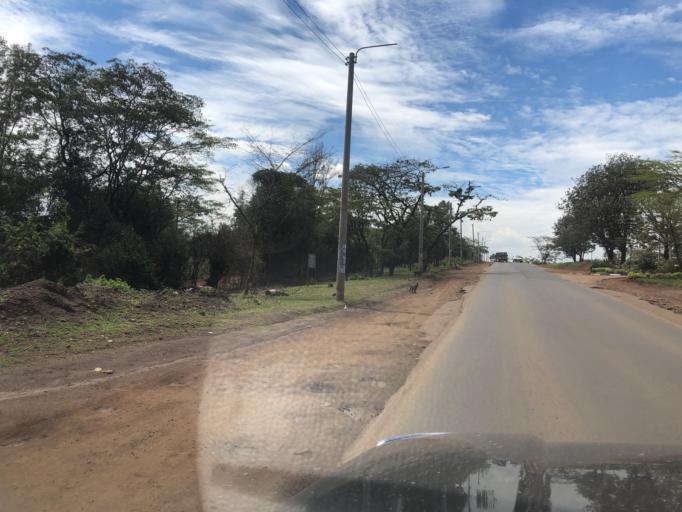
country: KE
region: Nairobi Area
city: Nairobi
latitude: -1.3650
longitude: 36.7663
